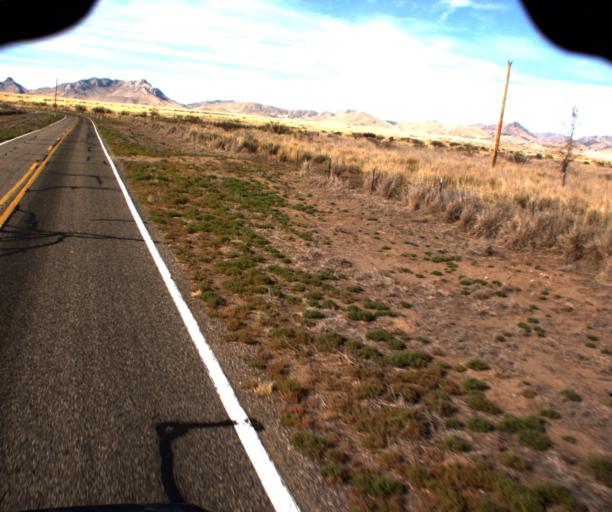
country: US
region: Arizona
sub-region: Cochise County
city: Willcox
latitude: 32.0193
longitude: -109.4400
